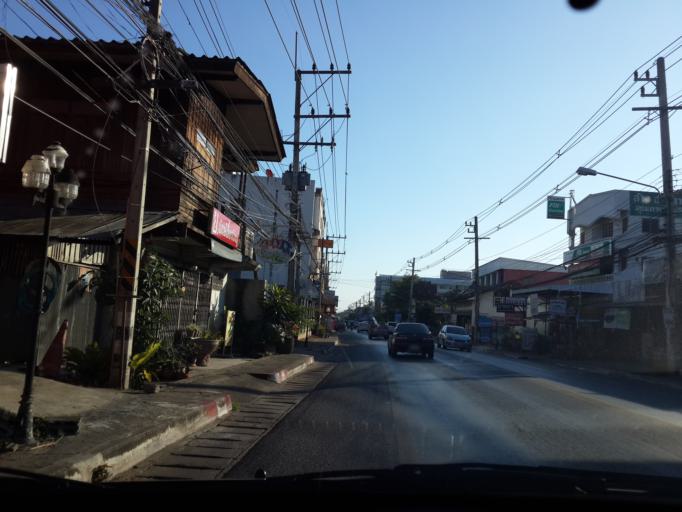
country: TH
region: Chiang Mai
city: Hang Dong
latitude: 18.6858
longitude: 98.9192
